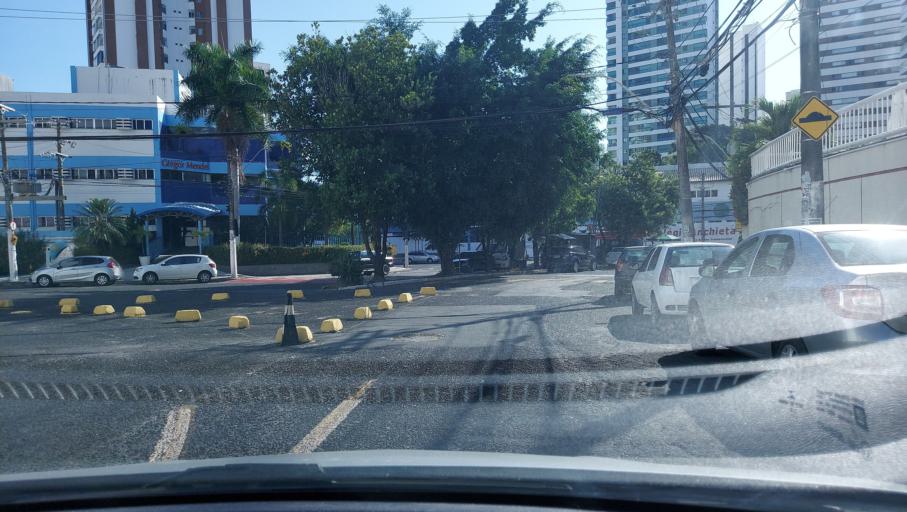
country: BR
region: Bahia
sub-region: Salvador
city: Salvador
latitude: -12.9889
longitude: -38.4523
